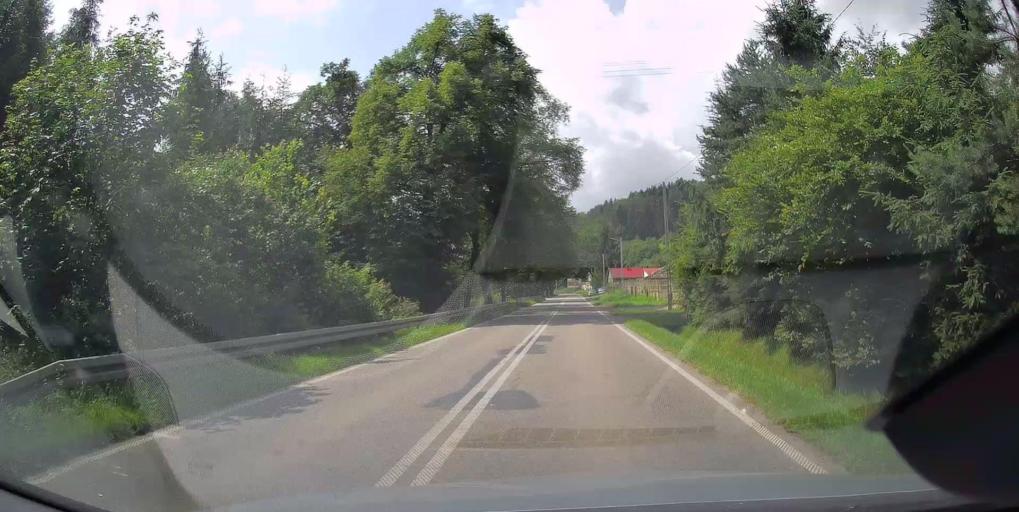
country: PL
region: Lesser Poland Voivodeship
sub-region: Powiat nowosadecki
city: Nowy Sacz
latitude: 49.6573
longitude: 20.7276
